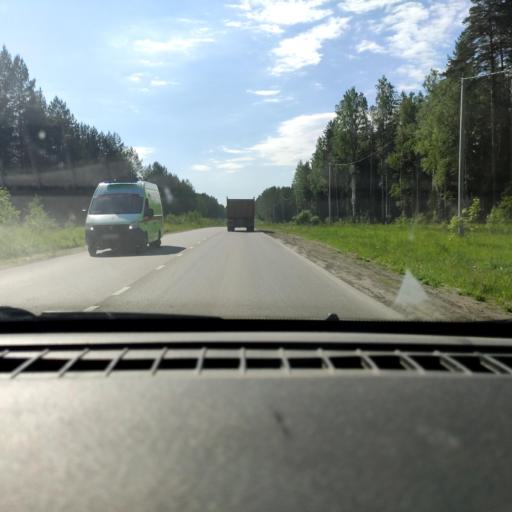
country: RU
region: Perm
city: Overyata
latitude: 58.0192
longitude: 55.8570
